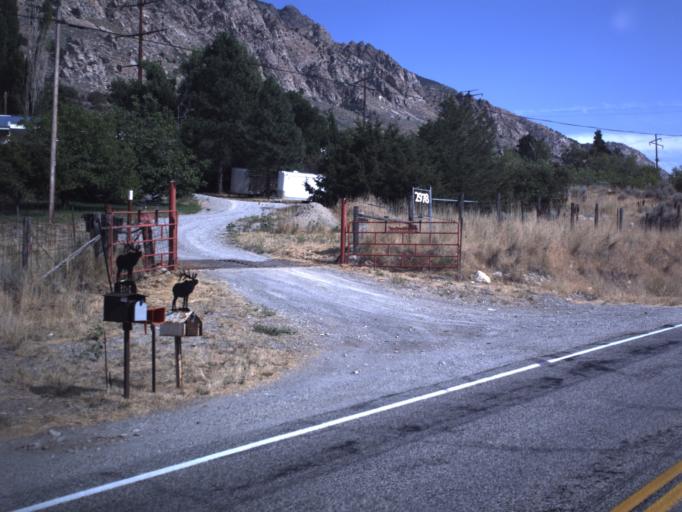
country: US
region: Utah
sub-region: Box Elder County
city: Brigham City
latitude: 41.5643
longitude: -112.0245
